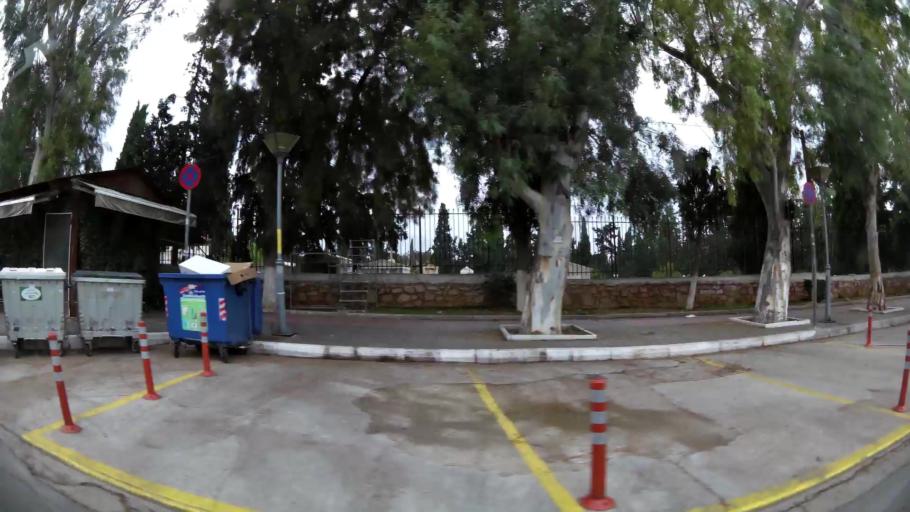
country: GR
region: Attica
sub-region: Nomarchia Athinas
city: Nea Smyrni
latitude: 37.9318
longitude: 23.7142
